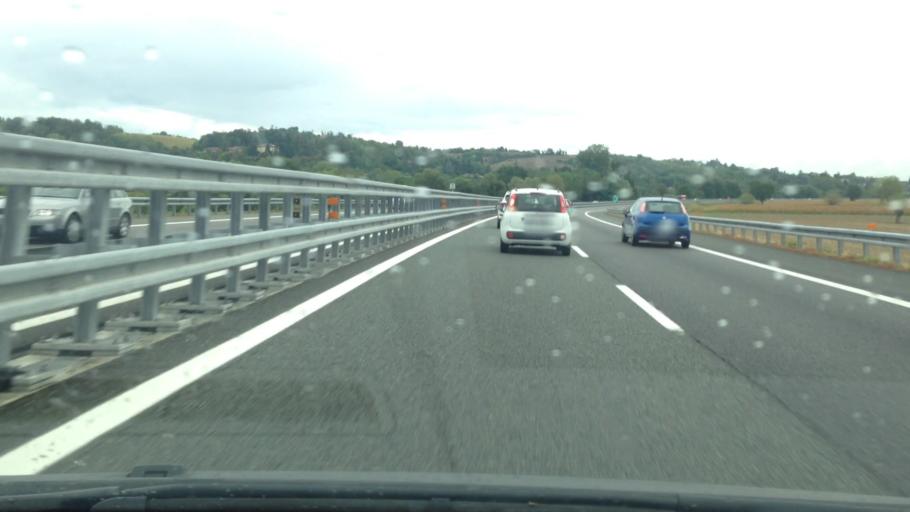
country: IT
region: Piedmont
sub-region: Provincia di Alessandria
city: Valle San Bartolomeo
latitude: 44.9452
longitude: 8.6393
